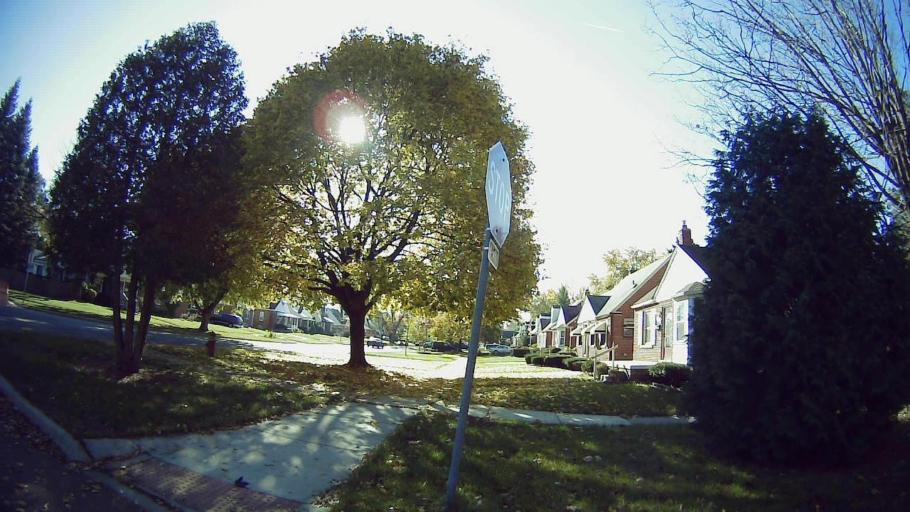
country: US
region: Michigan
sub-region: Wayne County
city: Dearborn Heights
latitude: 42.3489
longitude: -83.2648
